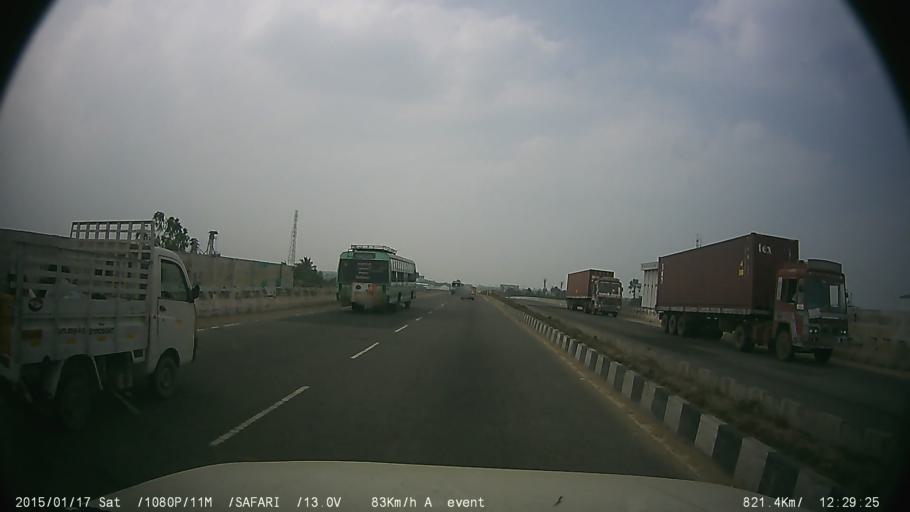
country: IN
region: Tamil Nadu
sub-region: Kancheepuram
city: Kanchipuram
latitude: 12.8747
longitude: 79.6909
